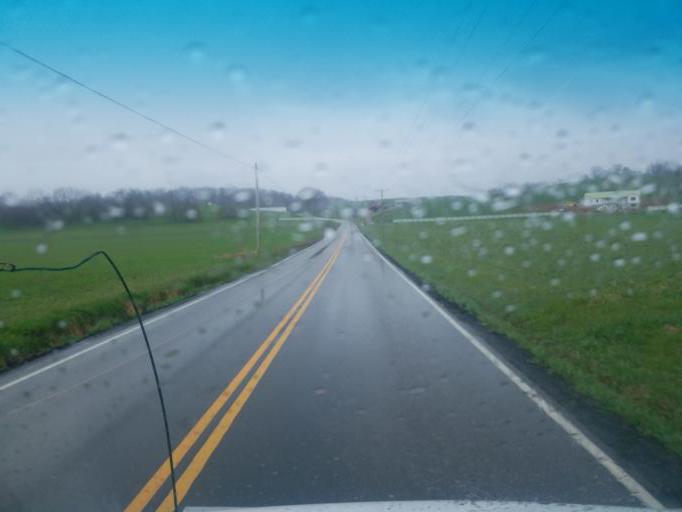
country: US
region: Ohio
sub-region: Holmes County
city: Millersburg
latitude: 40.6272
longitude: -81.9110
